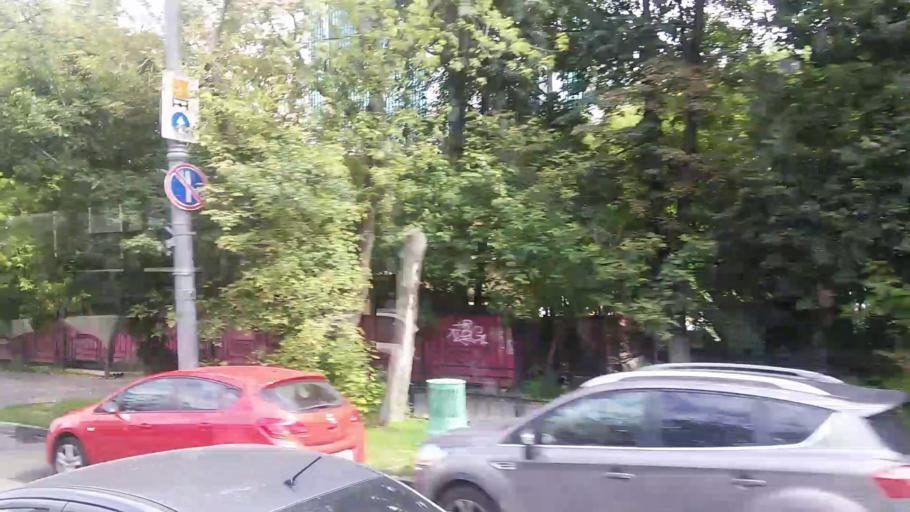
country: RU
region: Moscow
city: Novyye Cheremushki
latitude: 55.7006
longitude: 37.5774
